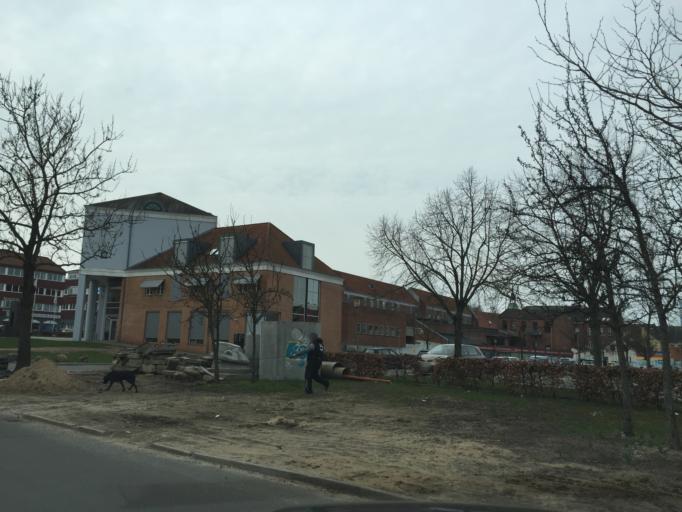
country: DK
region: South Denmark
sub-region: Kolding Kommune
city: Kolding
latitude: 55.4870
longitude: 9.4754
